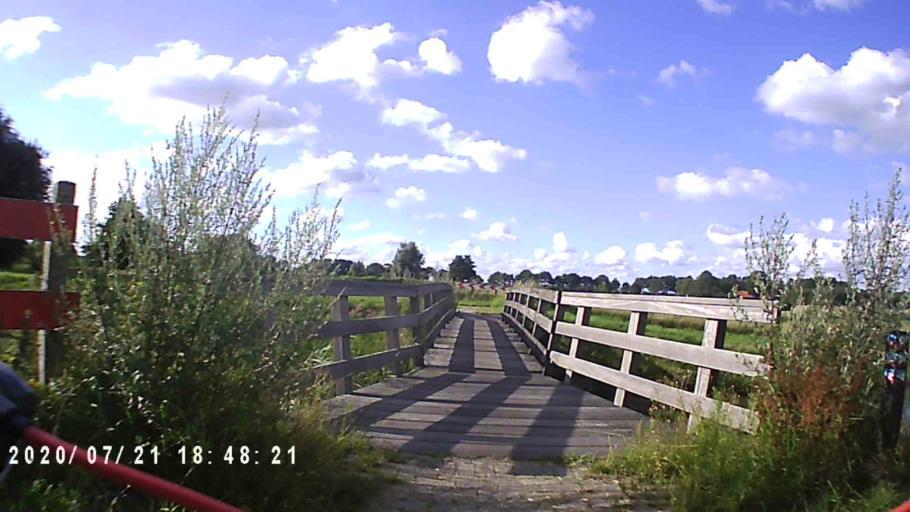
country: NL
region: Groningen
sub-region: Gemeente Hoogezand-Sappemeer
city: Hoogezand
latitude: 53.2161
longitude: 6.7479
